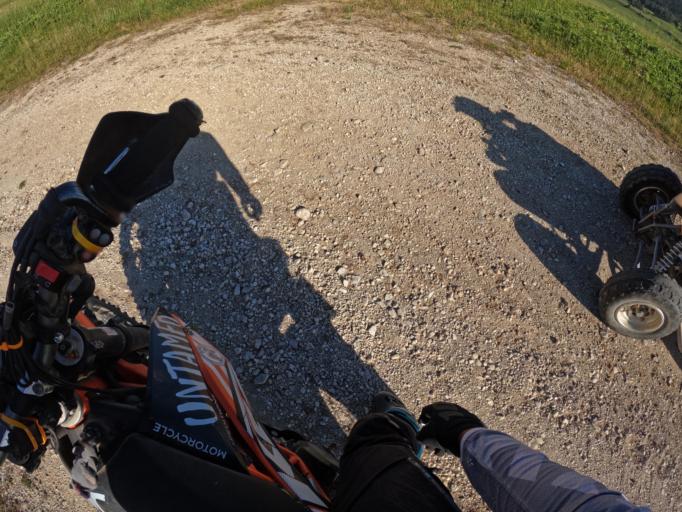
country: BA
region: Federation of Bosnia and Herzegovina
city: Glamoc
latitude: 44.2341
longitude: 16.8475
